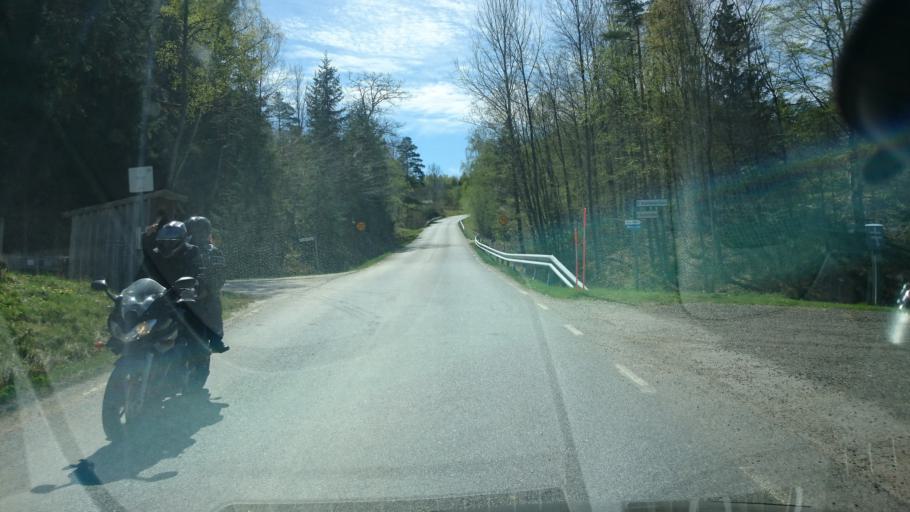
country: SE
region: Vaestra Goetaland
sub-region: Munkedals Kommun
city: Munkedal
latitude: 58.4253
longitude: 11.6942
